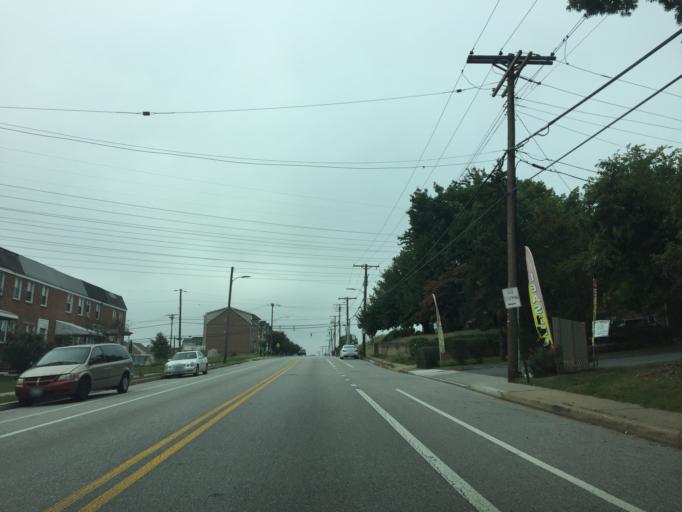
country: US
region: Maryland
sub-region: Baltimore County
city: Rosedale
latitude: 39.3221
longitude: -76.5406
